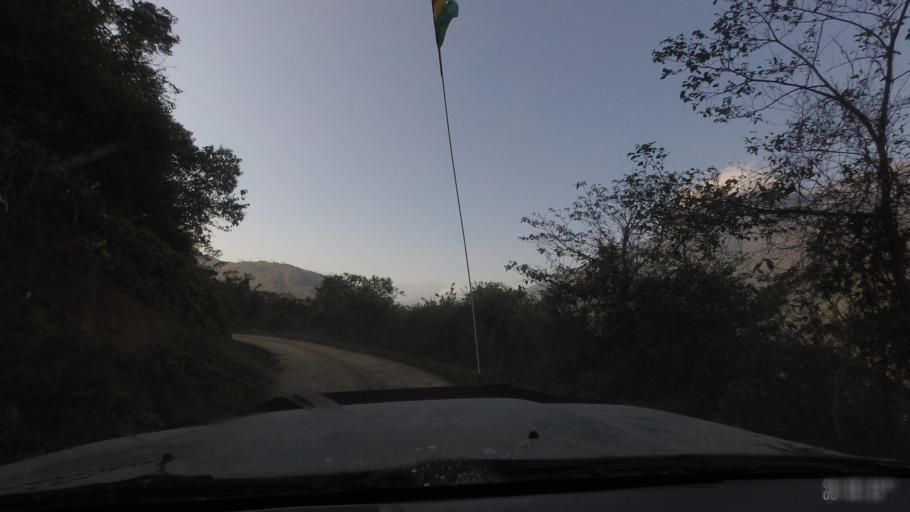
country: BO
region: La Paz
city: Quime
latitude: -16.5255
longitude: -66.7675
